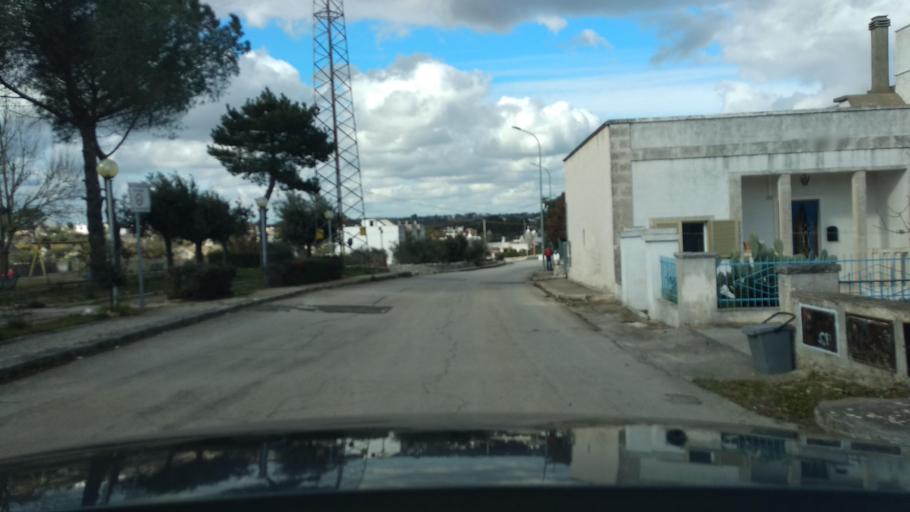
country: IT
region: Apulia
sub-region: Provincia di Brindisi
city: Cisternino
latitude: 40.7481
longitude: 17.4142
